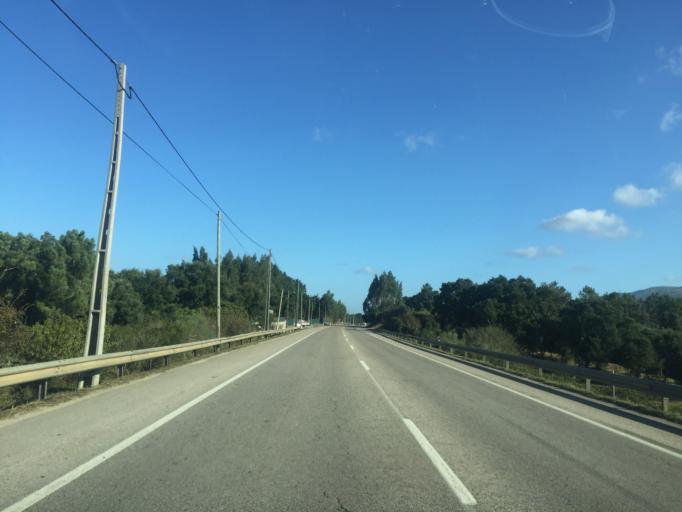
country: PT
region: Leiria
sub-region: Alcobaca
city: Aljubarrota
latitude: 39.5035
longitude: -8.9271
